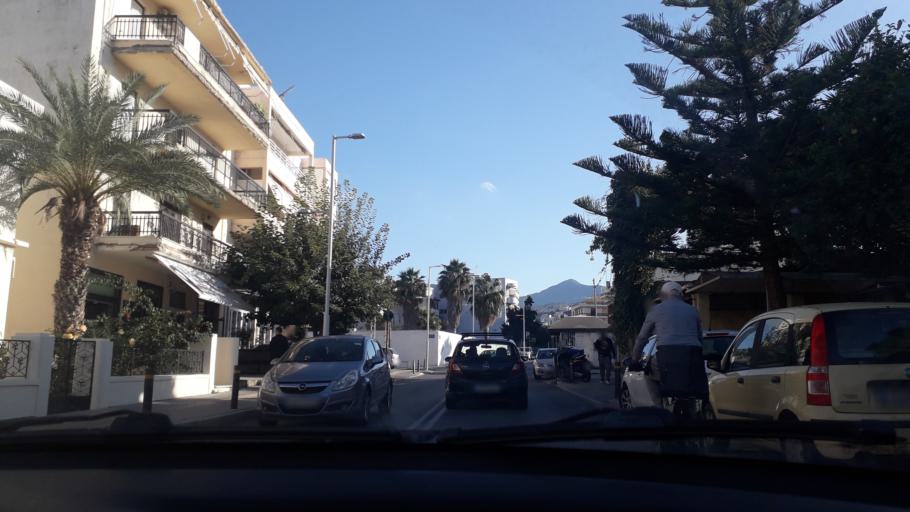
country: GR
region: Crete
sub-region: Nomos Rethymnis
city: Rethymno
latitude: 35.3664
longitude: 24.4700
